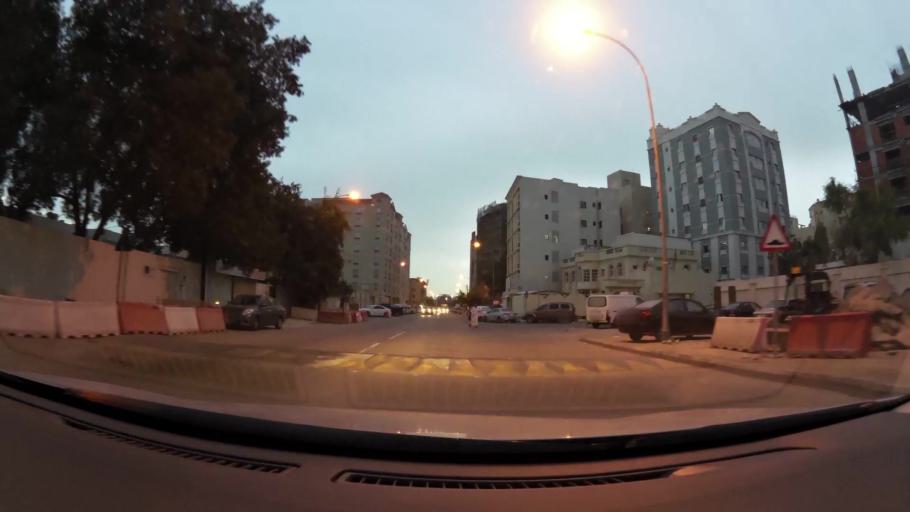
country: QA
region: Baladiyat ad Dawhah
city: Doha
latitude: 25.2693
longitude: 51.5223
